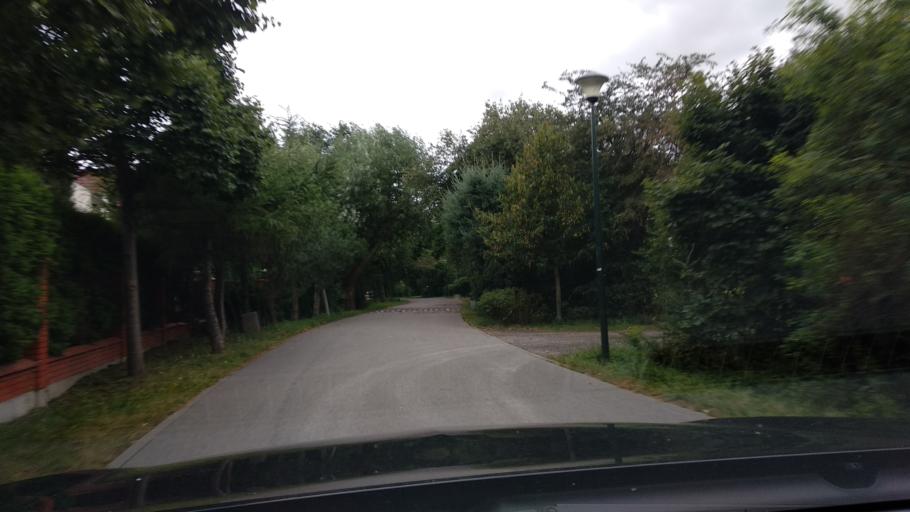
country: PL
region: Masovian Voivodeship
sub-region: Warszawa
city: Ursynow
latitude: 52.1335
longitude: 21.0478
